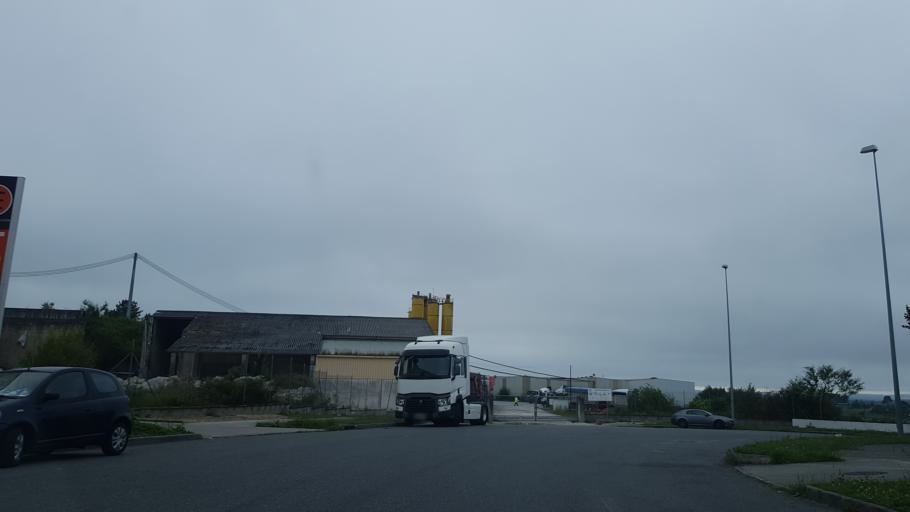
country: ES
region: Galicia
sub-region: Provincia de Lugo
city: Lugo
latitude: 43.0487
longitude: -7.5642
